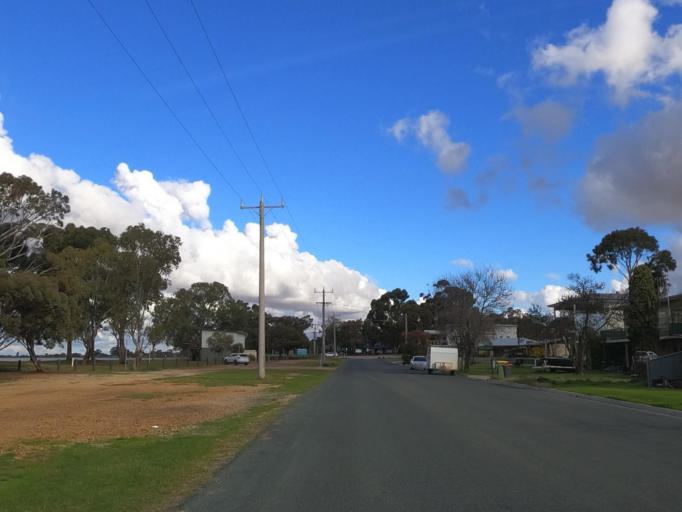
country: AU
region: Victoria
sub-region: Swan Hill
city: Swan Hill
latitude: -35.4484
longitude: 143.6274
